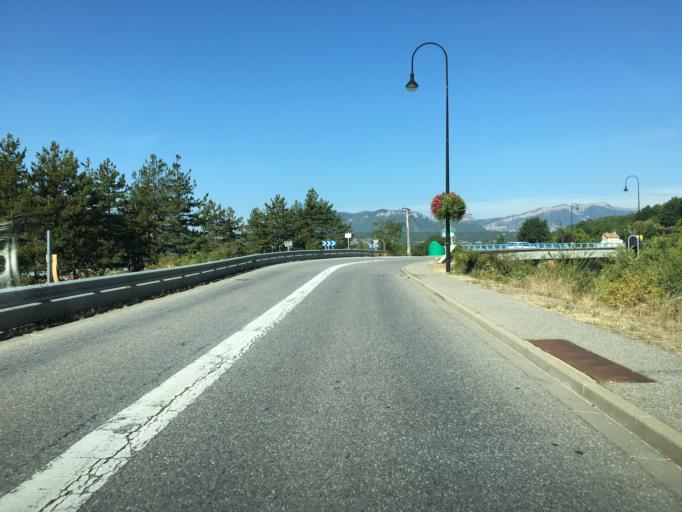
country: FR
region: Provence-Alpes-Cote d'Azur
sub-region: Departement des Hautes-Alpes
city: Laragne-Monteglin
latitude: 44.3167
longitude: 5.8147
